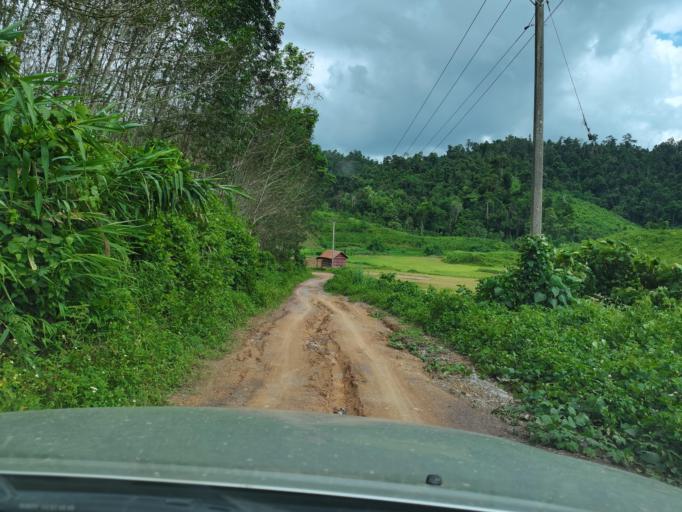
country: LA
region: Loungnamtha
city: Muang Long
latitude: 20.7012
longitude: 101.0165
